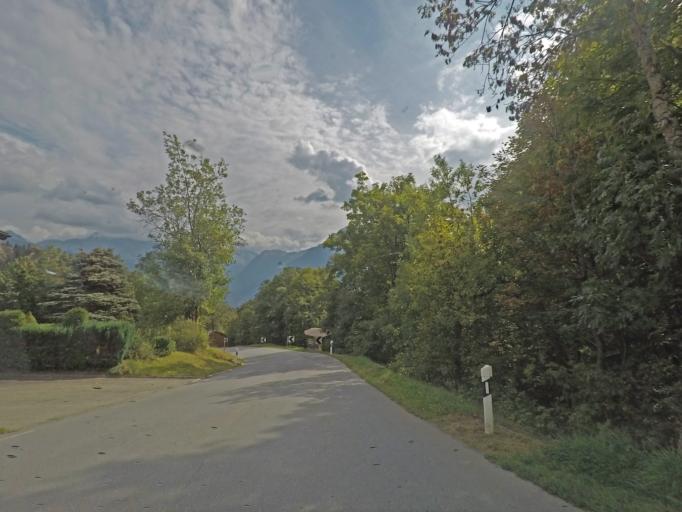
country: CH
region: Valais
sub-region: Brig District
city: Naters
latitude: 46.3481
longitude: 7.9811
